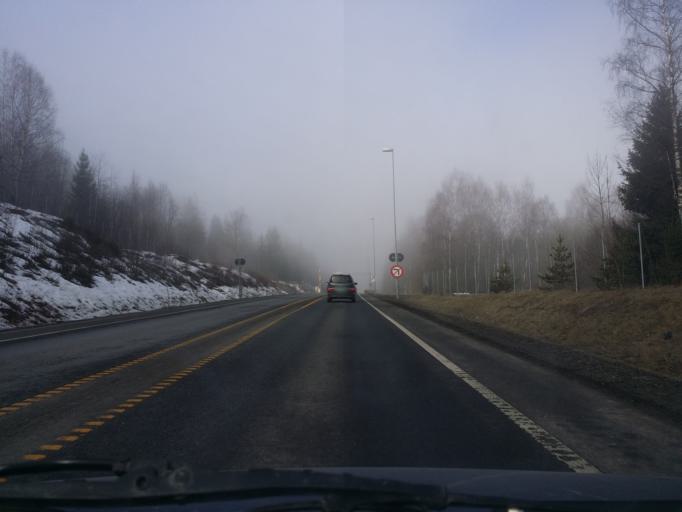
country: NO
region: Buskerud
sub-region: Drammen
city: Drammen
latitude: 59.7384
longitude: 10.1552
